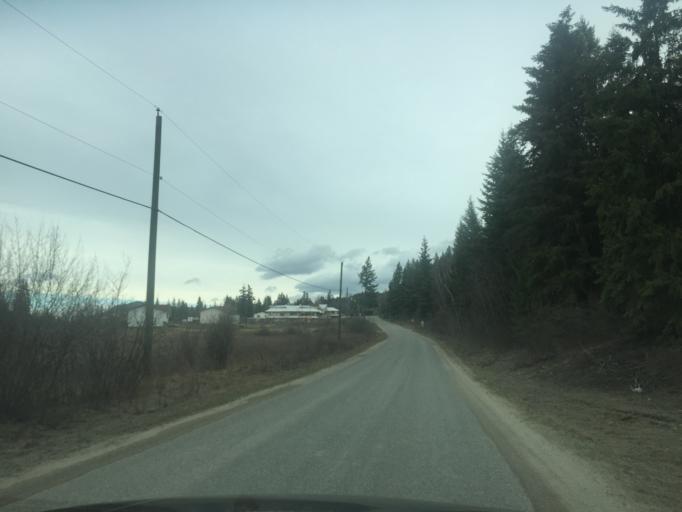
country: CA
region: British Columbia
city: Kamloops
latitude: 51.3142
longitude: -120.1500
